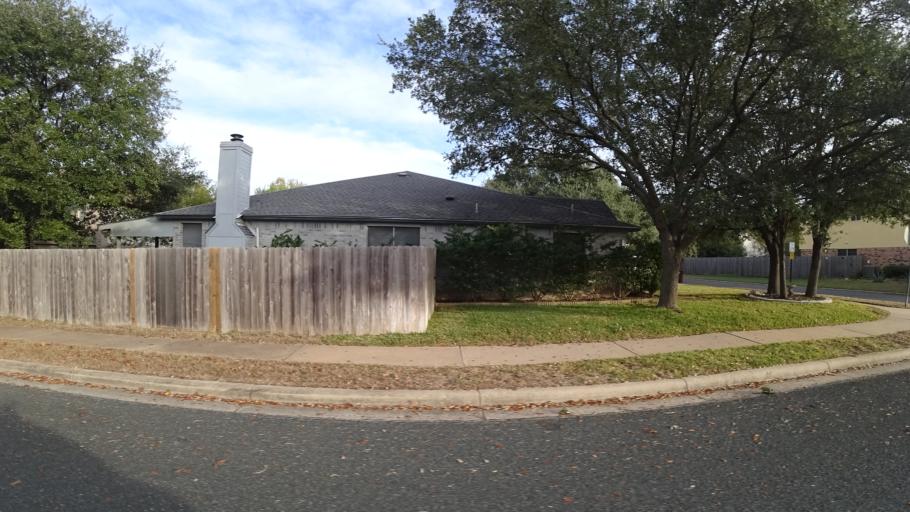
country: US
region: Texas
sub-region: Williamson County
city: Brushy Creek
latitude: 30.5148
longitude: -97.7267
